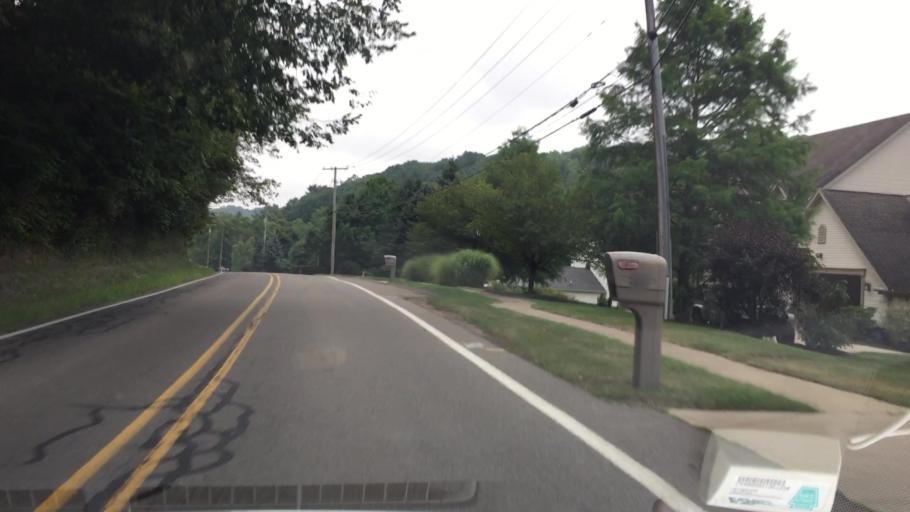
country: US
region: Pennsylvania
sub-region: Allegheny County
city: Franklin Park
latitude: 40.6045
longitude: -80.0746
